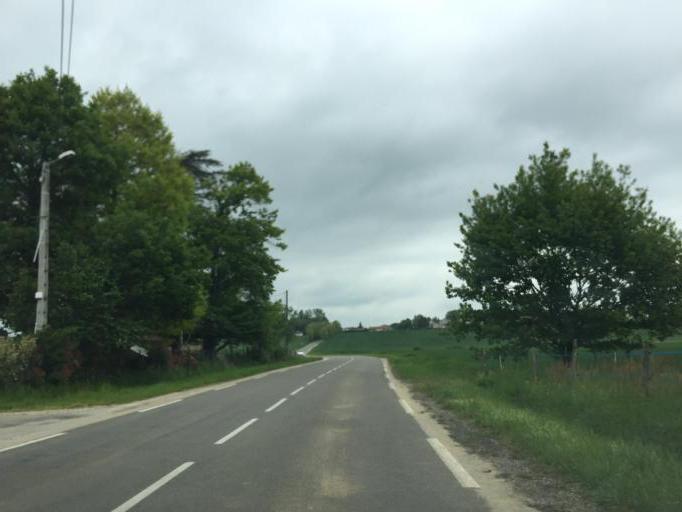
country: FR
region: Rhone-Alpes
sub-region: Departement de l'Ain
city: Tramoyes
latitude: 45.8626
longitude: 4.9594
